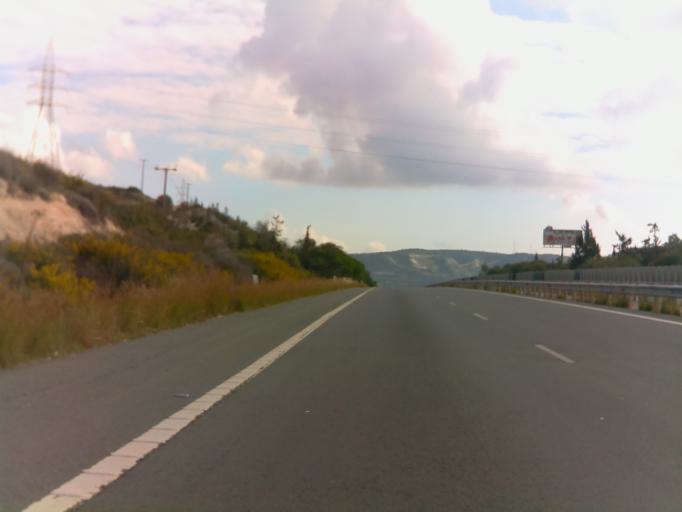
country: CY
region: Limassol
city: Pyrgos
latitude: 34.7195
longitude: 33.1844
